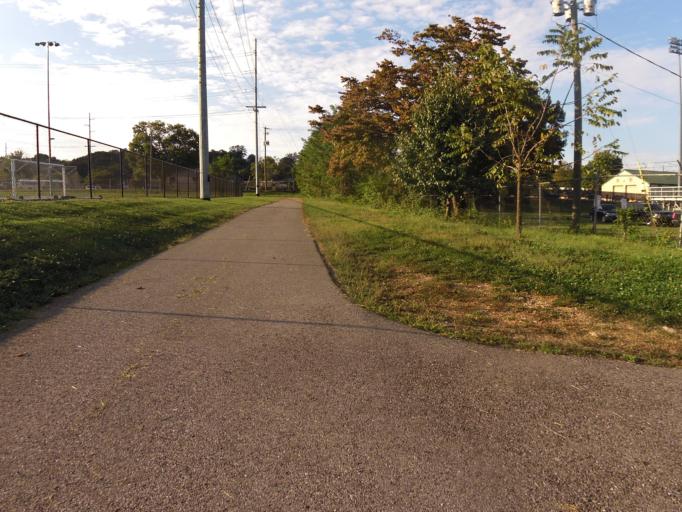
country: US
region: Tennessee
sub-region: Knox County
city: Knoxville
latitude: 35.9459
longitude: -83.9759
